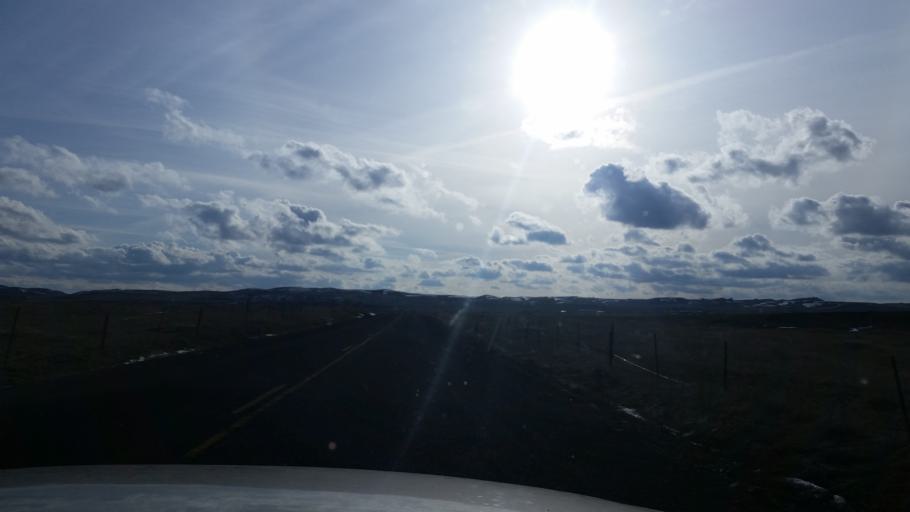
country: US
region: Washington
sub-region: Spokane County
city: Cheney
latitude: 47.2683
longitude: -117.6632
